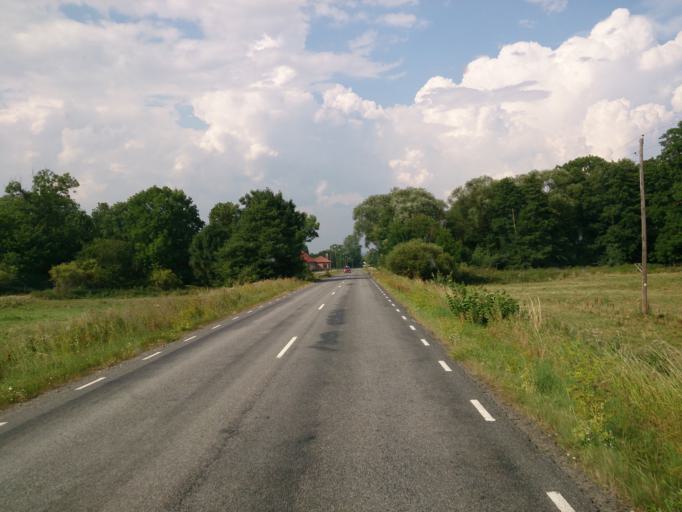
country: SE
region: Skane
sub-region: Kristianstads Kommun
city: Fjalkinge
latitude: 56.0828
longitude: 14.3499
